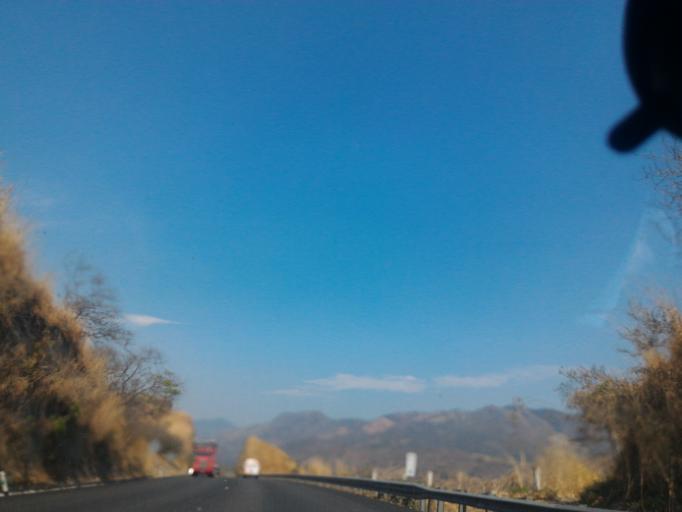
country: MX
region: Jalisco
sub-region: Tonila
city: San Marcos
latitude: 19.4534
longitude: -103.4688
